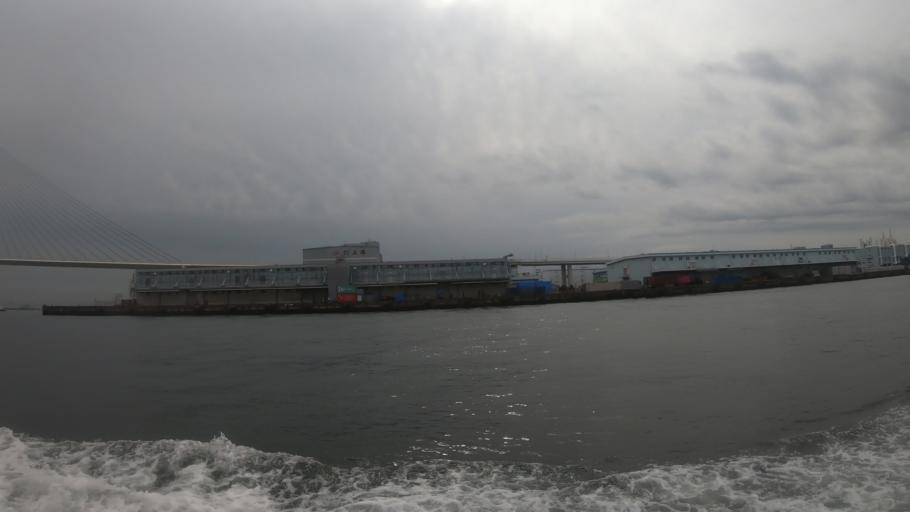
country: JP
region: Kanagawa
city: Yokohama
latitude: 35.4727
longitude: 139.6903
